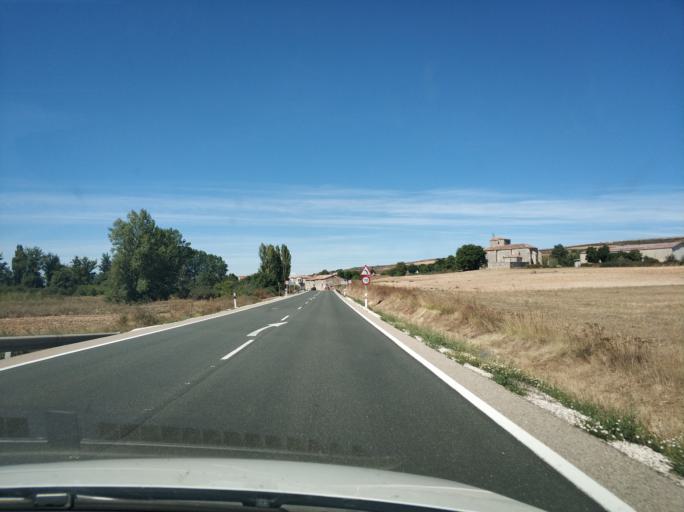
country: ES
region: Castille and Leon
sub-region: Provincia de Burgos
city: Tubilla del Agua
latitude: 42.6445
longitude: -3.8809
